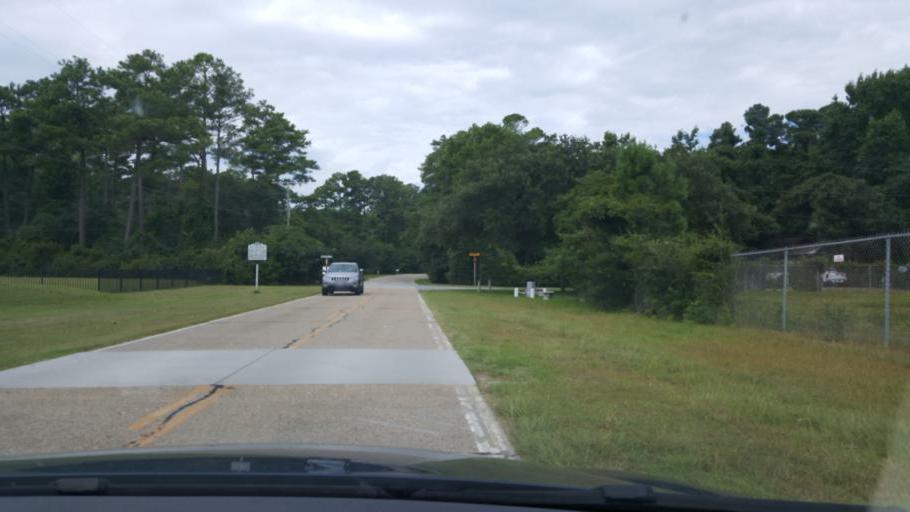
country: US
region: North Carolina
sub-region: Dare County
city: Manteo
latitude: 35.9191
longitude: -75.7045
